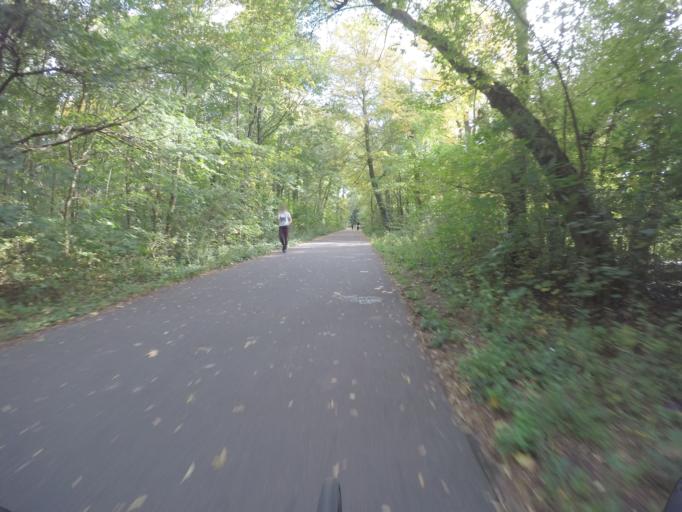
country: DE
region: Berlin
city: Pankow
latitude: 52.5758
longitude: 13.3874
